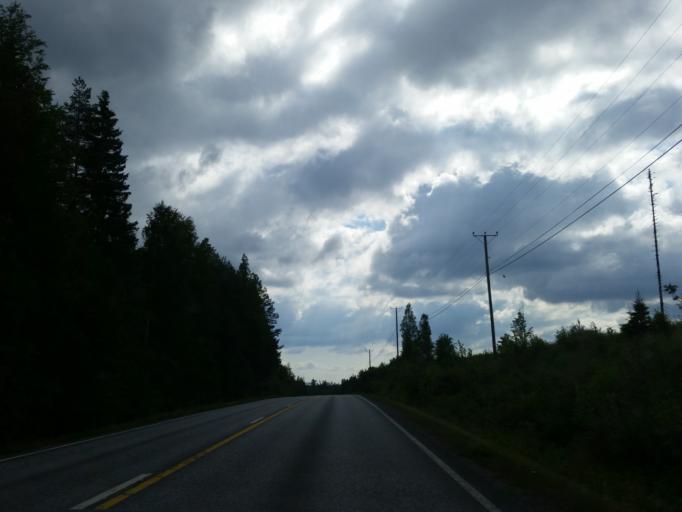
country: FI
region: Northern Savo
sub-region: Kuopio
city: Kuopio
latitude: 62.8423
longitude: 27.4835
